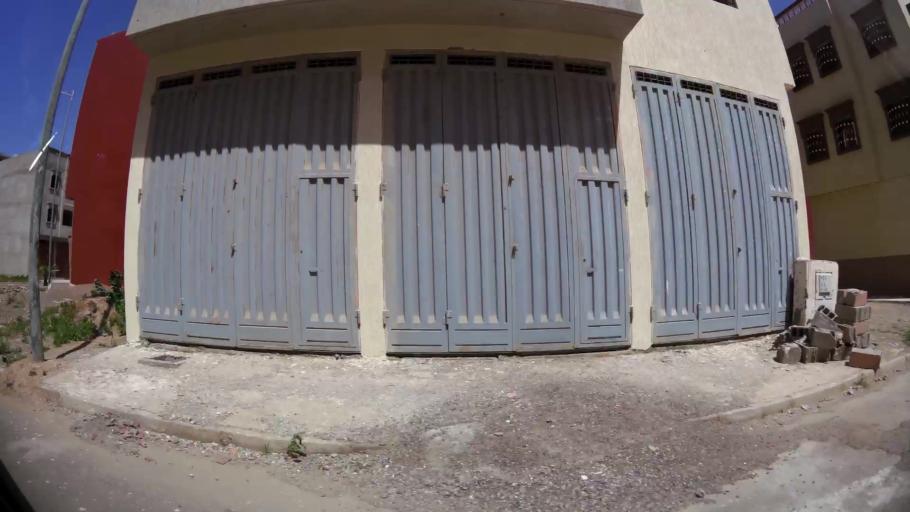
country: MA
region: Souss-Massa-Draa
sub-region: Inezgane-Ait Mellou
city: Inezgane
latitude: 30.3452
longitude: -9.5195
